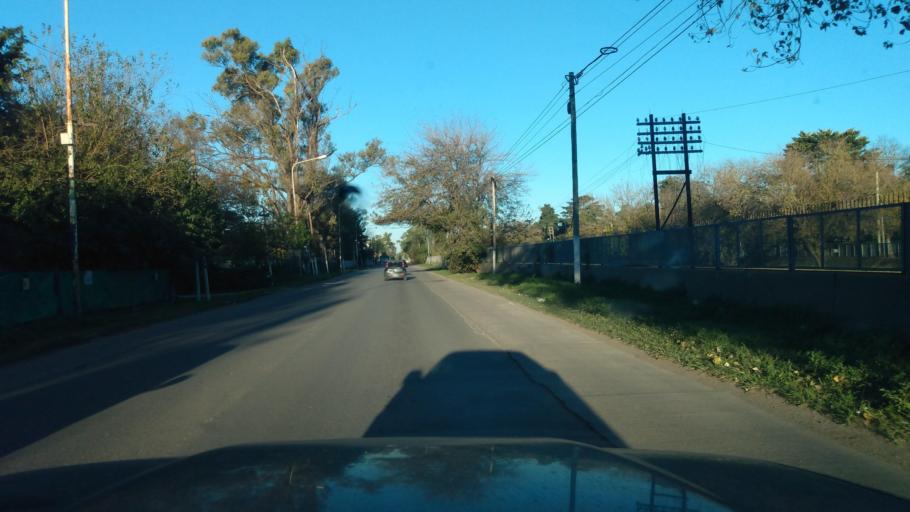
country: AR
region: Buenos Aires
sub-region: Partido de Merlo
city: Merlo
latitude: -34.6417
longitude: -58.8208
